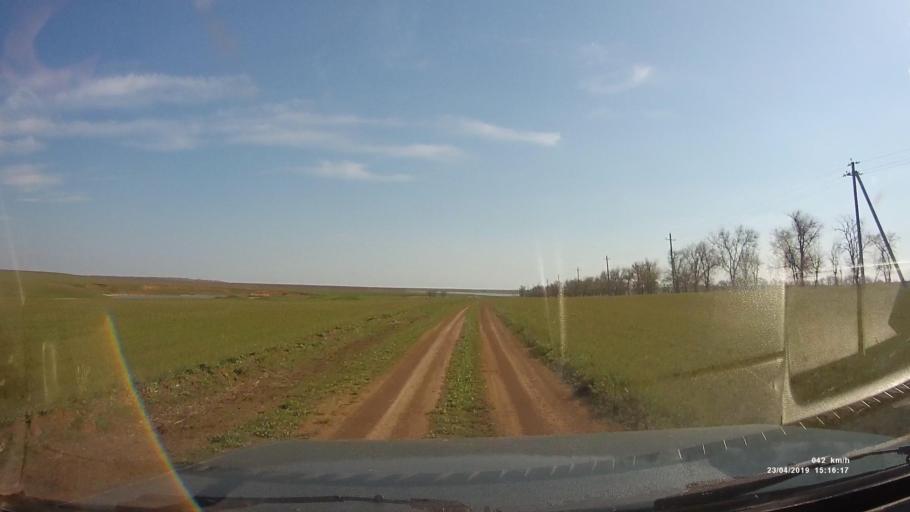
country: RU
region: Rostov
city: Remontnoye
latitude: 46.5345
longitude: 42.9698
